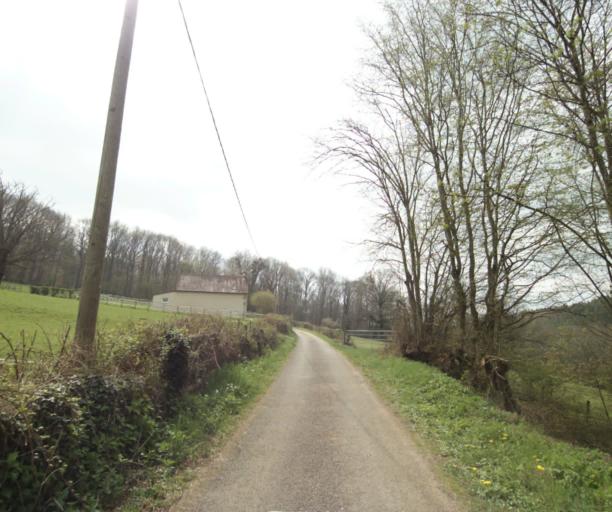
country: FR
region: Bourgogne
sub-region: Departement de Saone-et-Loire
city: Charolles
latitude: 46.3911
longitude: 4.2720
